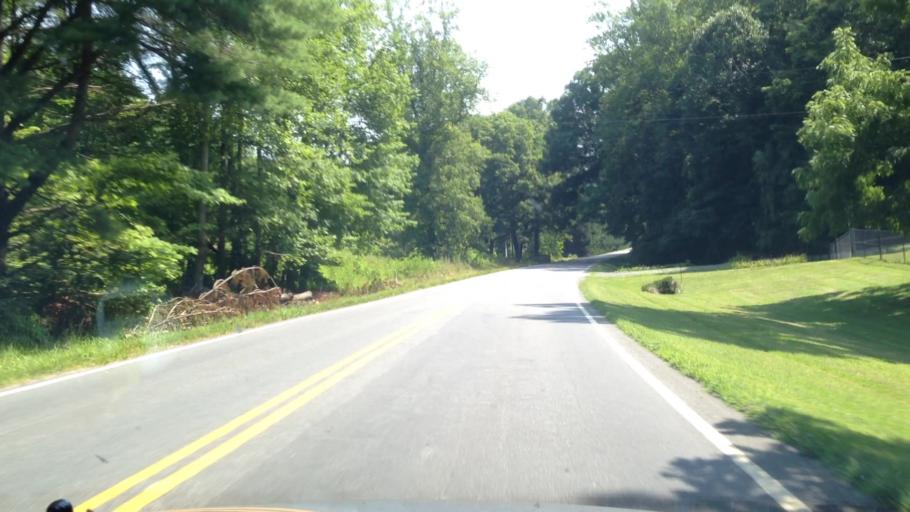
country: US
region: North Carolina
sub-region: Surry County
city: Flat Rock
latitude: 36.5737
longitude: -80.4512
